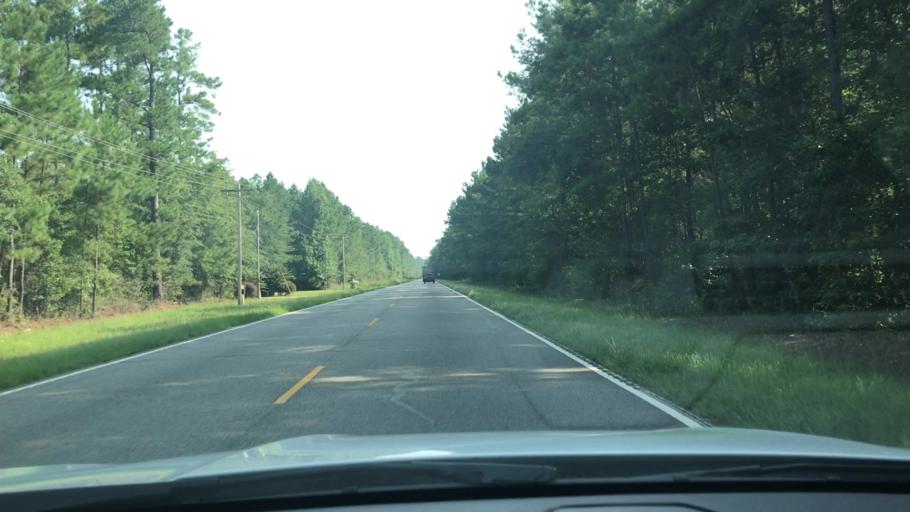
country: US
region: South Carolina
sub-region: Georgetown County
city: Georgetown
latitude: 33.4861
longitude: -79.2671
